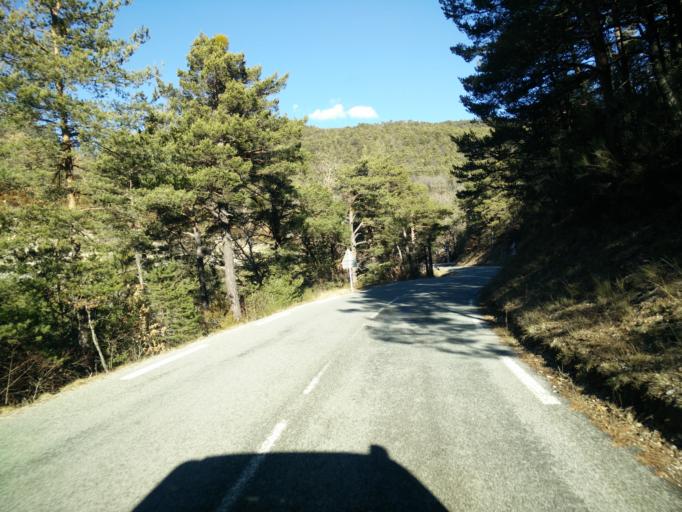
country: FR
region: Provence-Alpes-Cote d'Azur
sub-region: Departement des Alpes-de-Haute-Provence
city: Castellane
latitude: 43.7753
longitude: 6.4480
